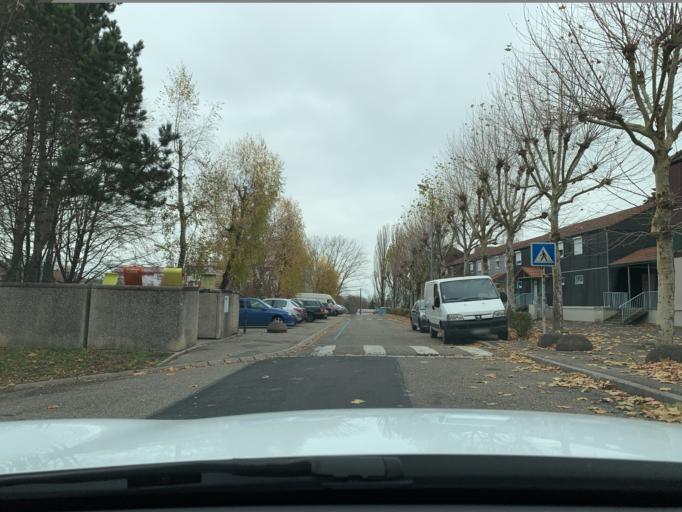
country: FR
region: Lorraine
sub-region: Departement de la Moselle
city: Sarreguemines
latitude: 49.0994
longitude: 7.0472
